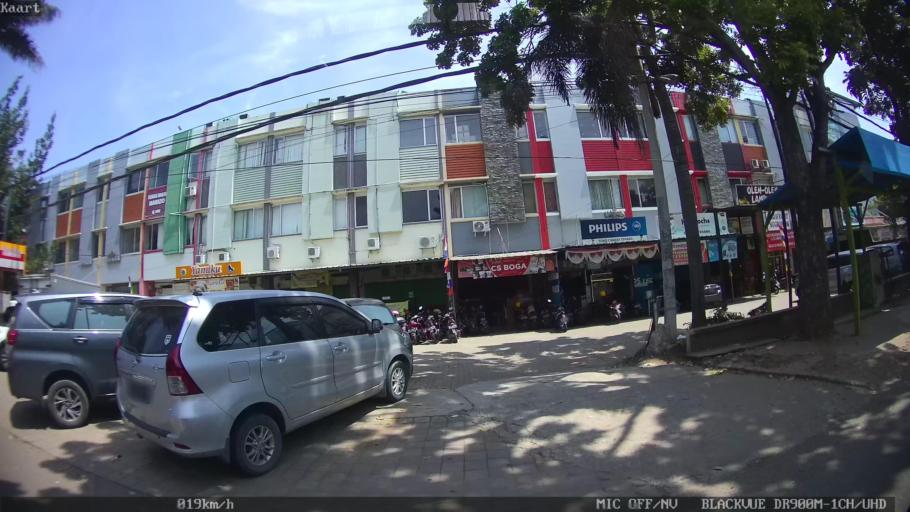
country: ID
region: Lampung
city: Kedaton
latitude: -5.3829
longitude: 105.2803
